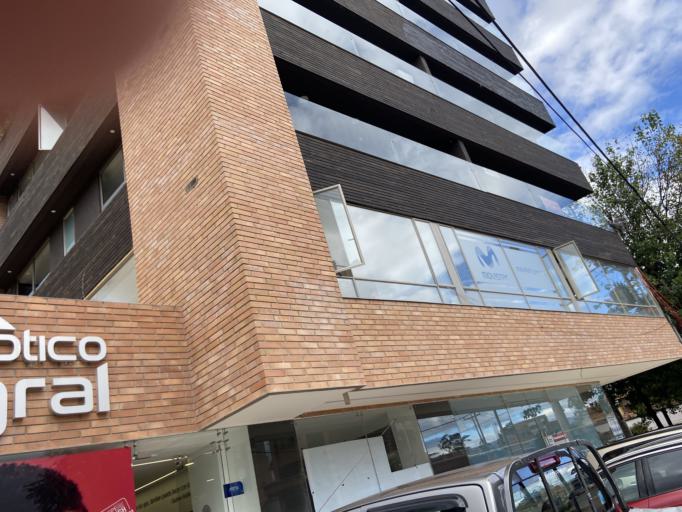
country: EC
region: Azuay
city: Cuenca
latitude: -2.8908
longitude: -79.0255
